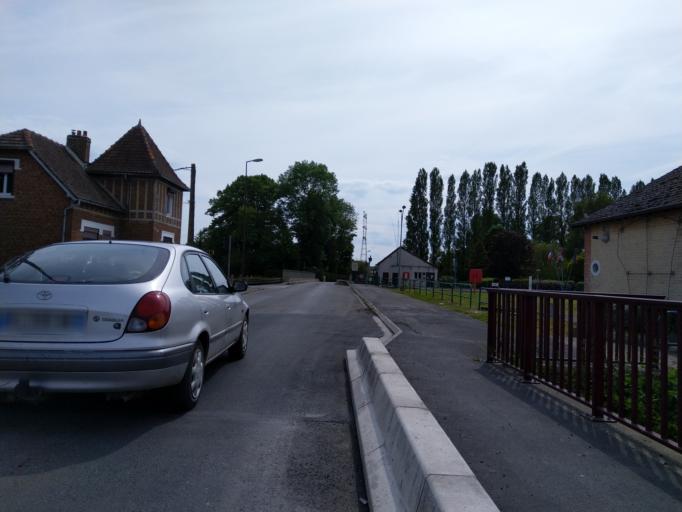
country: FR
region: Picardie
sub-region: Departement de l'Aisne
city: Boue
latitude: 50.0017
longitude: 3.6819
